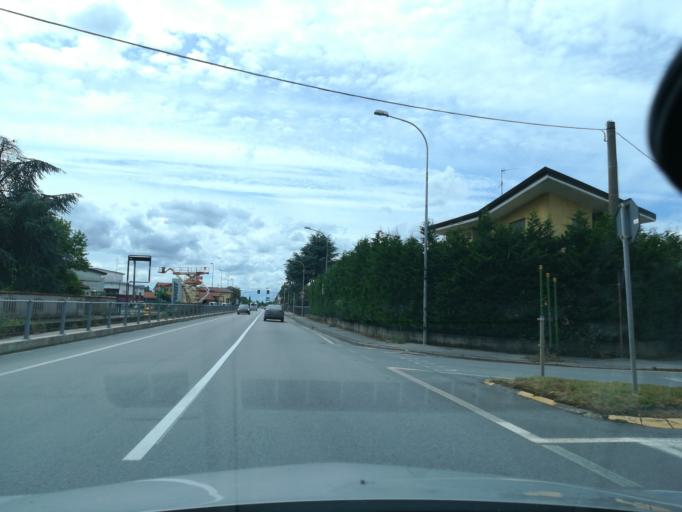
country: IT
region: Lombardy
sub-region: Provincia di Bergamo
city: Antegnate
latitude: 45.4866
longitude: 9.7937
